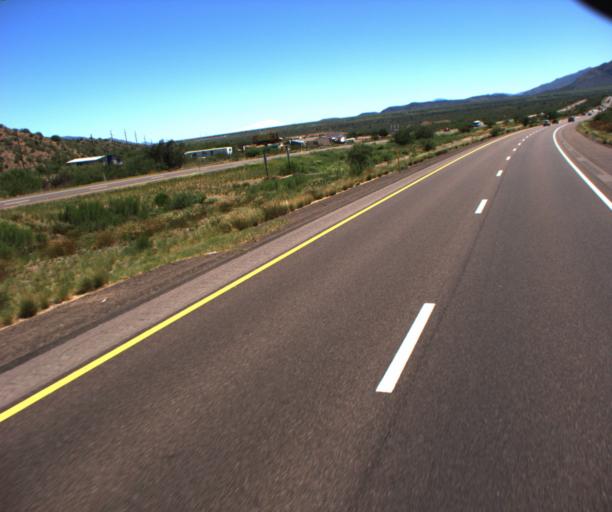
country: US
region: Arizona
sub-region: Gila County
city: Payson
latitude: 34.0923
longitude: -111.3538
